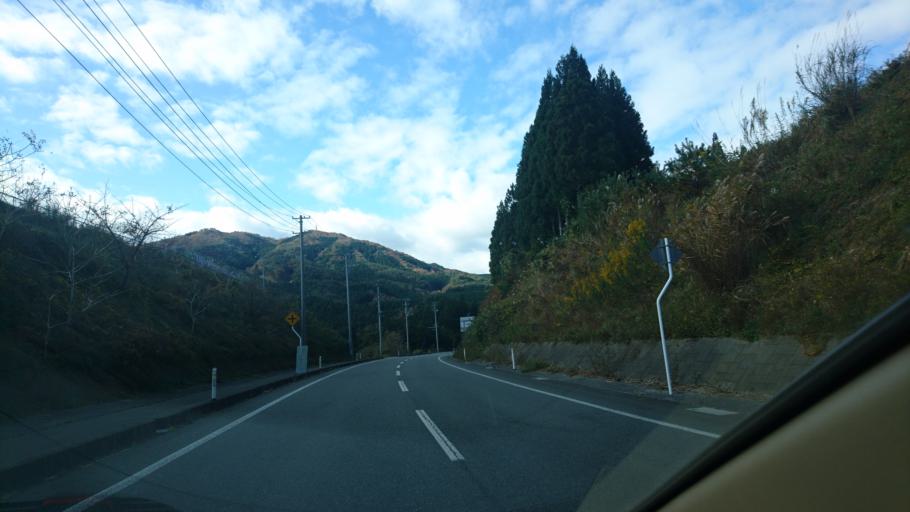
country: JP
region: Iwate
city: Ofunato
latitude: 39.0283
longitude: 141.7102
